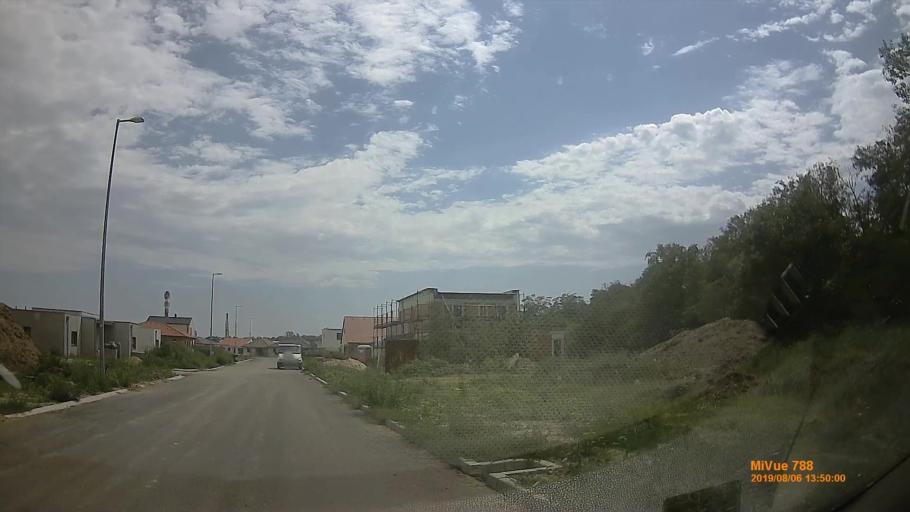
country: HU
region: Vas
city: Szombathely
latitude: 47.2520
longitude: 16.5982
